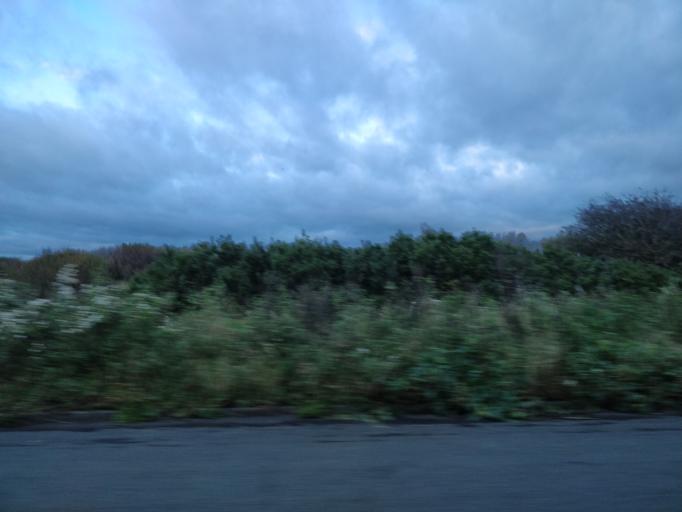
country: GB
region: England
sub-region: Sefton
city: Southport
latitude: 53.6647
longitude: -2.9899
